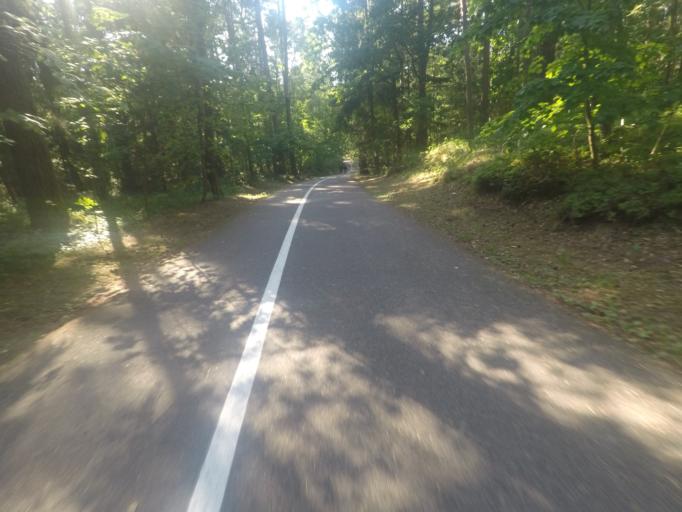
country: LT
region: Klaipedos apskritis
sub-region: Klaipeda
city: Klaipeda
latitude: 55.5456
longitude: 21.1156
